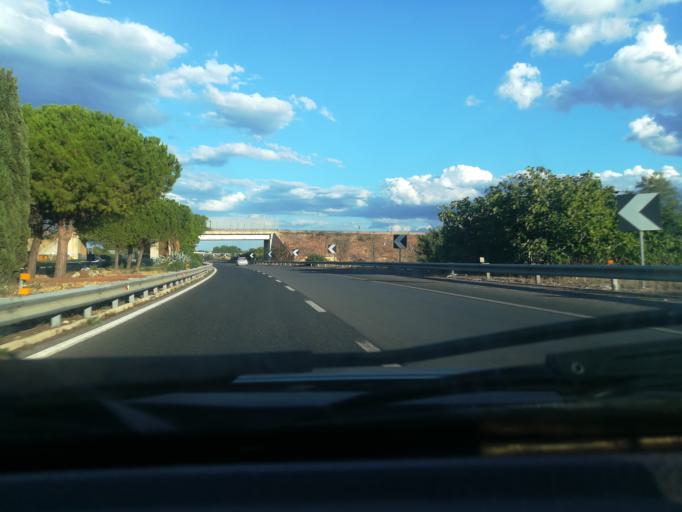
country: IT
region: Apulia
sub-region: Provincia di Bari
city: Mola di Bari
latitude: 41.0483
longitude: 17.0792
